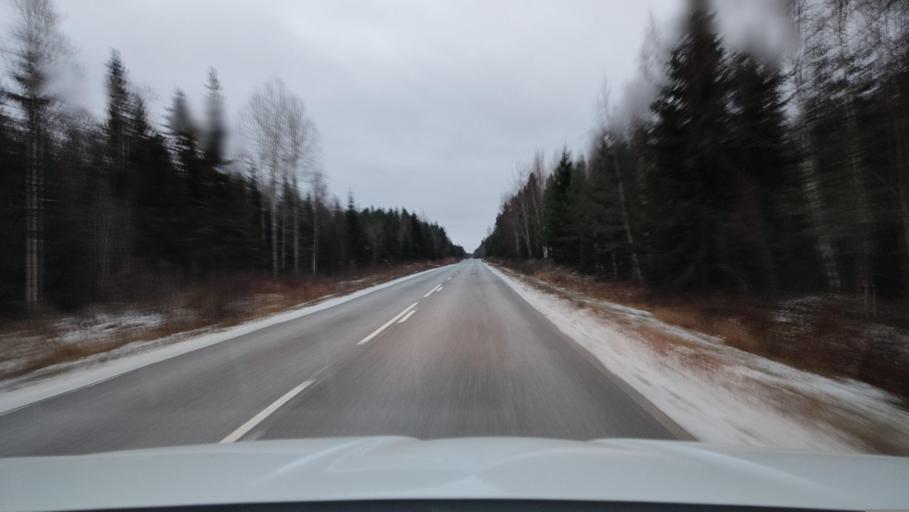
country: FI
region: Ostrobothnia
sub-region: Vaasa
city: Replot
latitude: 63.2622
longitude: 21.3606
